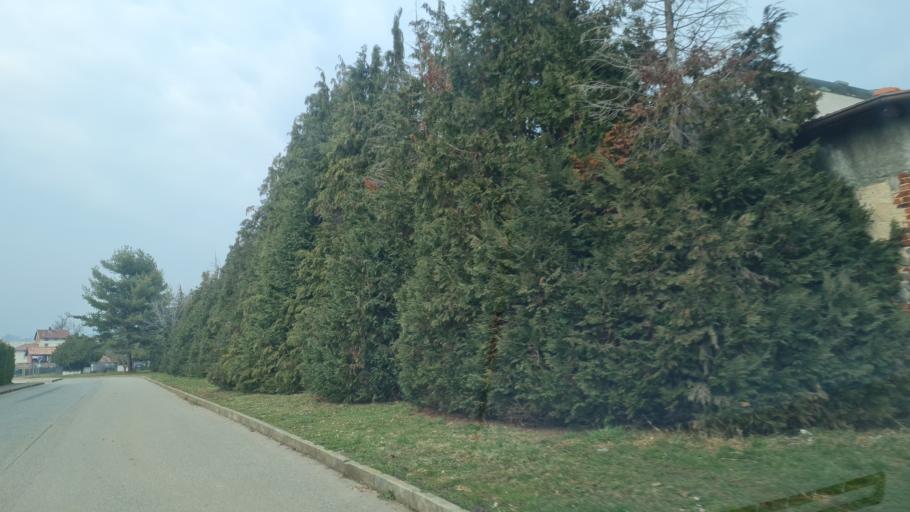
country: IT
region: Piedmont
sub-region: Provincia di Biella
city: Occhieppo Inferiore
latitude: 45.5511
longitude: 8.0269
